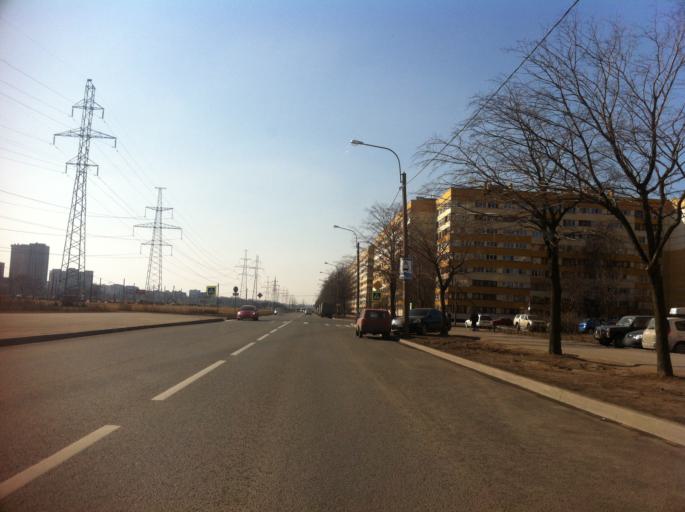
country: RU
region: St.-Petersburg
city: Uritsk
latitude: 59.8470
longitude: 30.1864
